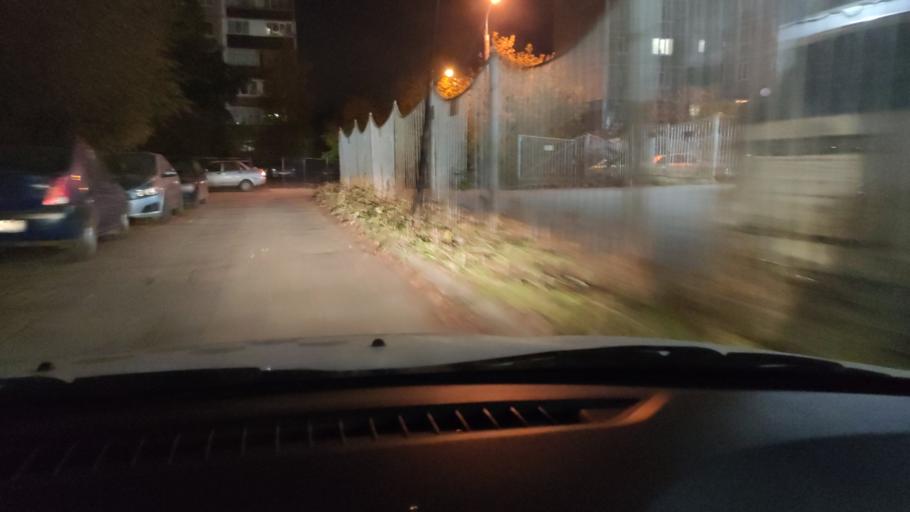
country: RU
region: Perm
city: Kondratovo
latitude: 57.9991
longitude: 56.1546
